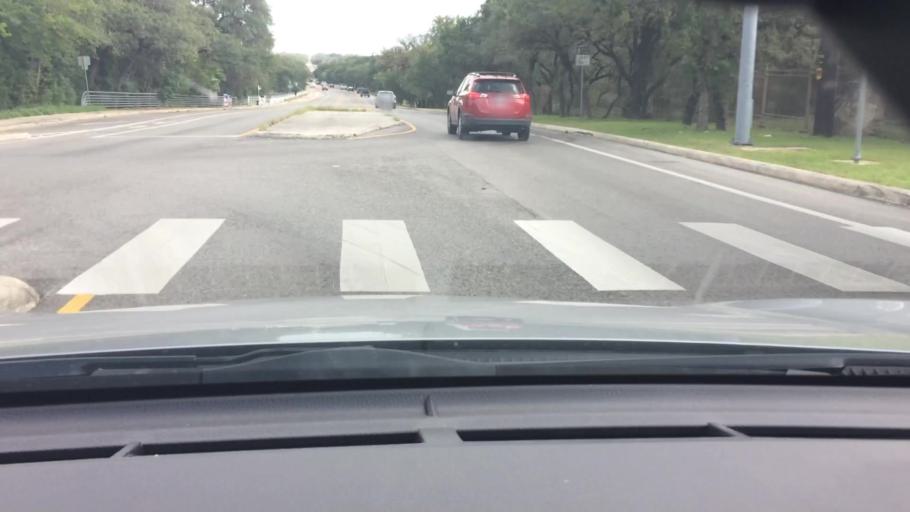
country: US
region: Texas
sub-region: Bexar County
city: Shavano Park
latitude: 29.5567
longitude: -98.5483
